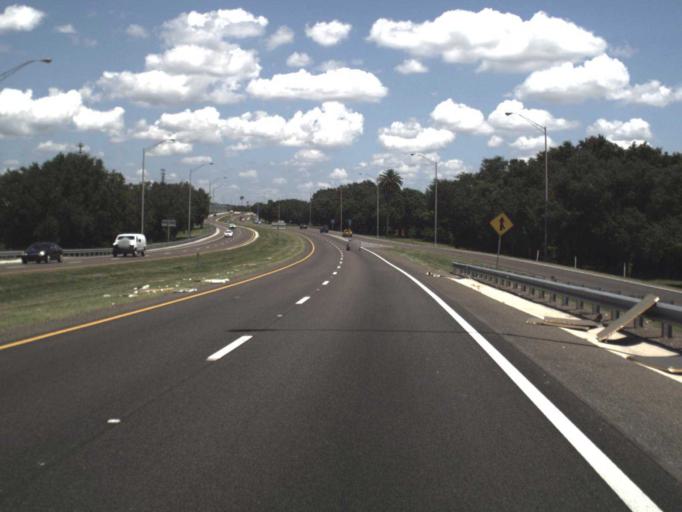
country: US
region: Florida
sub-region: Hillsborough County
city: Tampa
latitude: 27.8976
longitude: -82.5053
